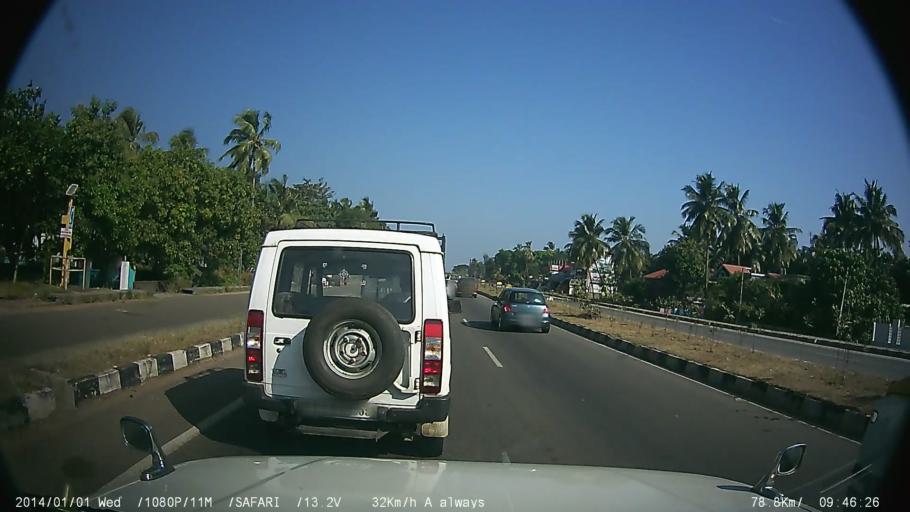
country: IN
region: Kerala
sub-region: Thrissur District
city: Trichur
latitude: 10.4692
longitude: 76.2577
